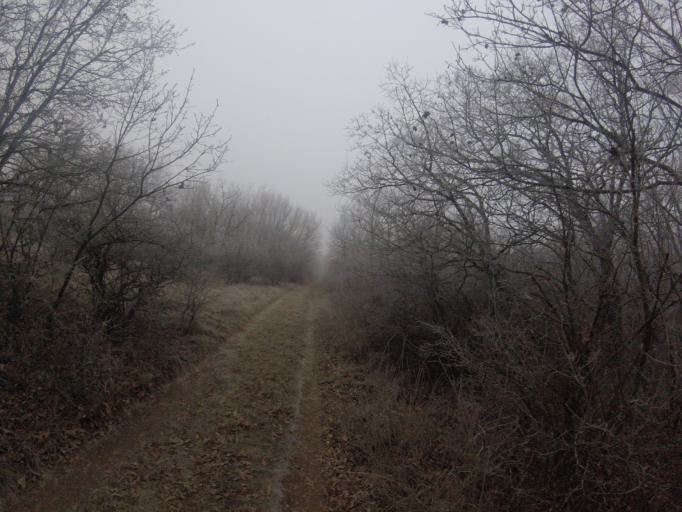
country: HU
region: Fejer
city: Csakvar
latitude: 47.3786
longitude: 18.4107
